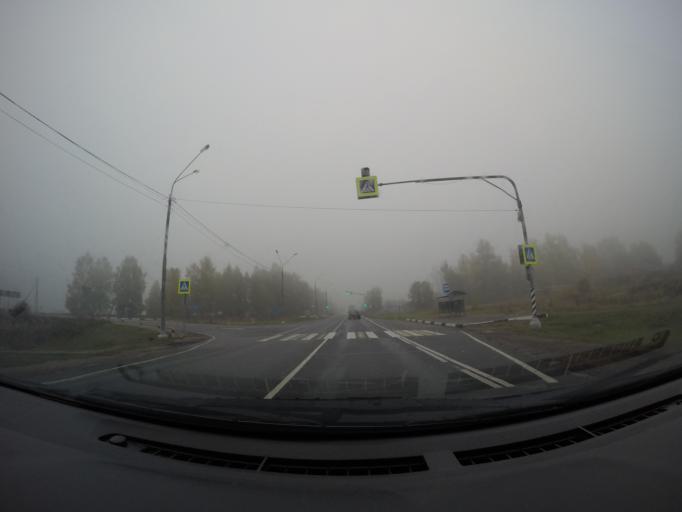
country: RU
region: Moskovskaya
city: Ruza
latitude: 55.7726
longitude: 36.2658
